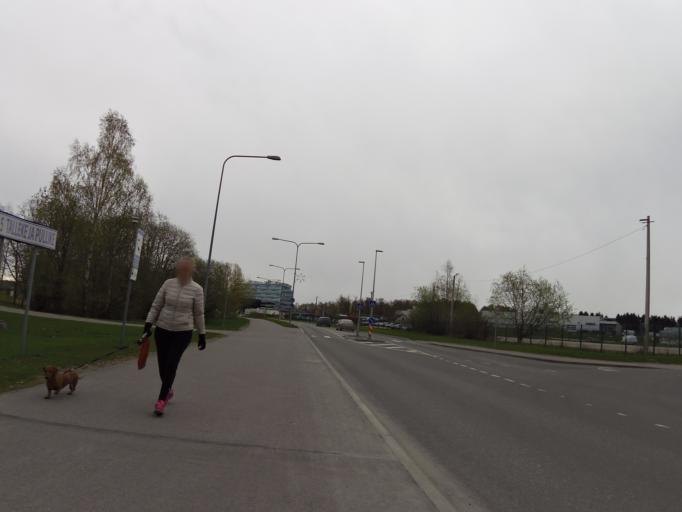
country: EE
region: Harju
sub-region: Saue vald
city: Laagri
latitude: 59.4288
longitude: 24.6549
